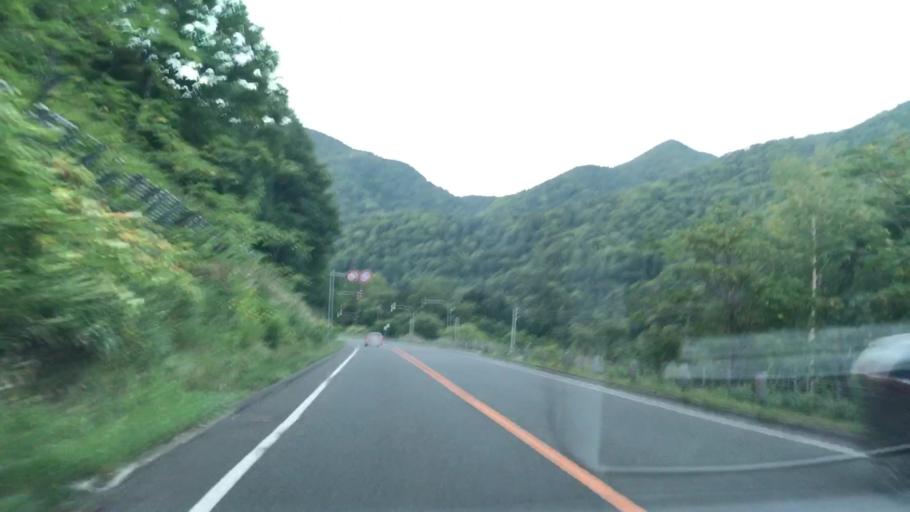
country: JP
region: Hokkaido
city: Sapporo
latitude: 42.9139
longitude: 141.1224
